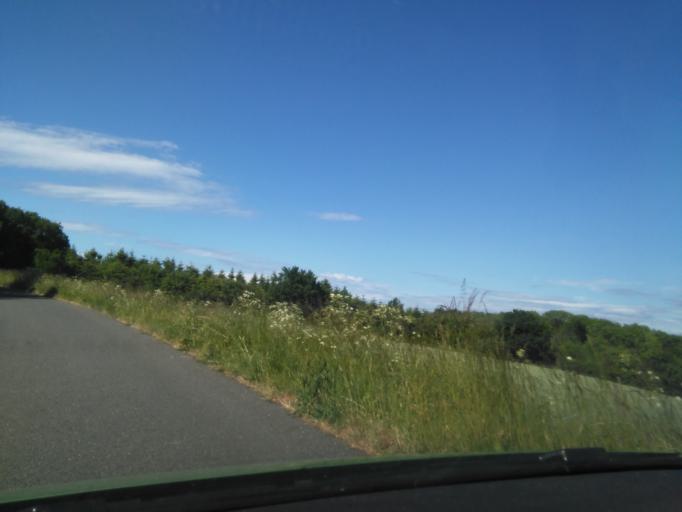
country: DK
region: Capital Region
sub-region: Bornholm Kommune
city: Nexo
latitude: 55.0670
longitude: 15.0833
